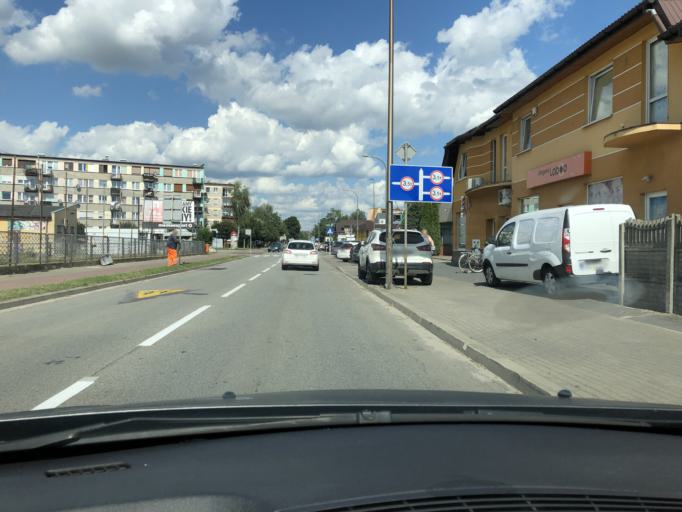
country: PL
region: Lodz Voivodeship
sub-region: Powiat wieruszowski
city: Wieruszow
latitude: 51.2959
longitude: 18.1610
